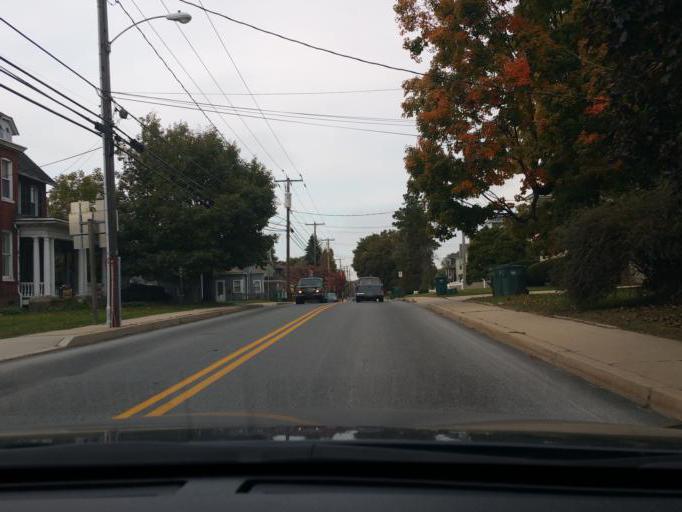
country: US
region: Pennsylvania
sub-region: Lancaster County
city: Quarryville
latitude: 39.8968
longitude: -76.1650
